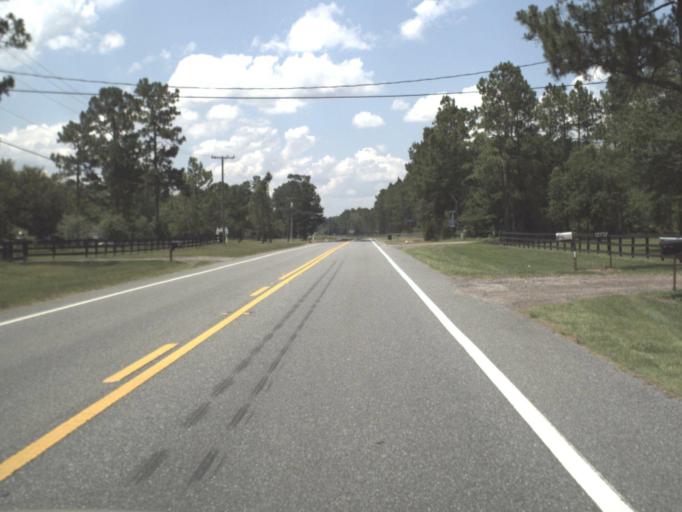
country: US
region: Florida
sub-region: Baker County
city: Macclenny
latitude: 30.3126
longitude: -82.1250
